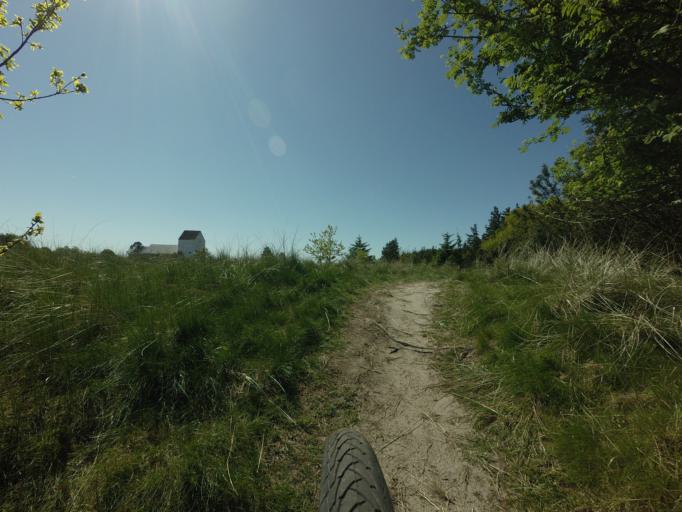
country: DK
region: North Denmark
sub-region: Jammerbugt Kommune
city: Pandrup
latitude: 57.2522
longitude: 9.6168
